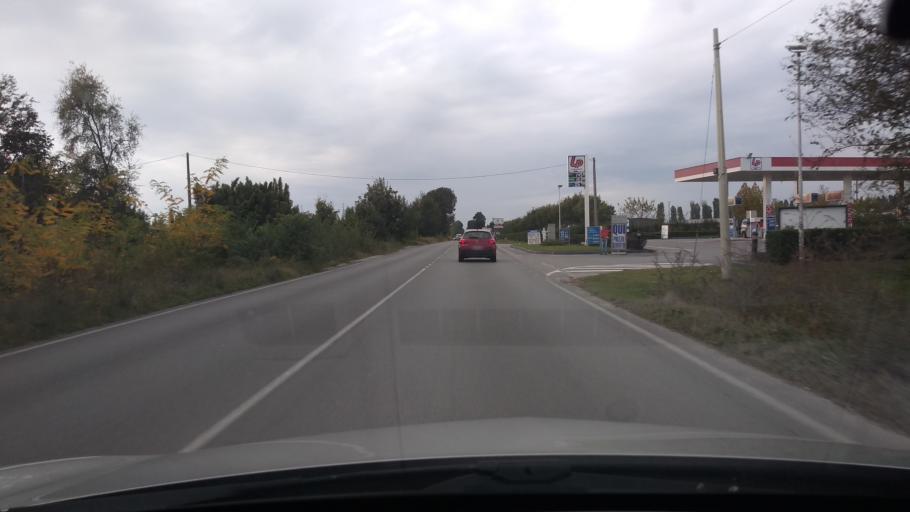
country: IT
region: Lombardy
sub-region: Provincia di Bergamo
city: Cologno al Serio
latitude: 45.5876
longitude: 9.7291
